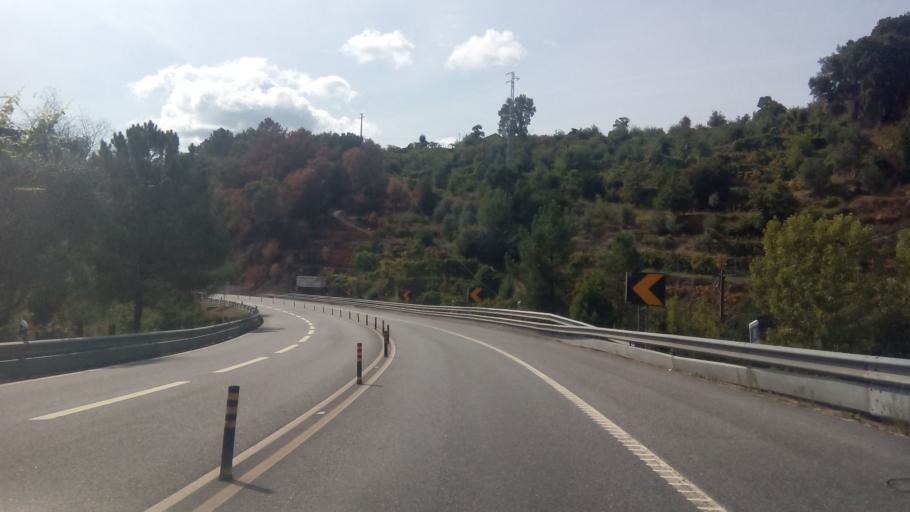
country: PT
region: Porto
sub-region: Amarante
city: Amarante
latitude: 41.2645
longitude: -8.0278
